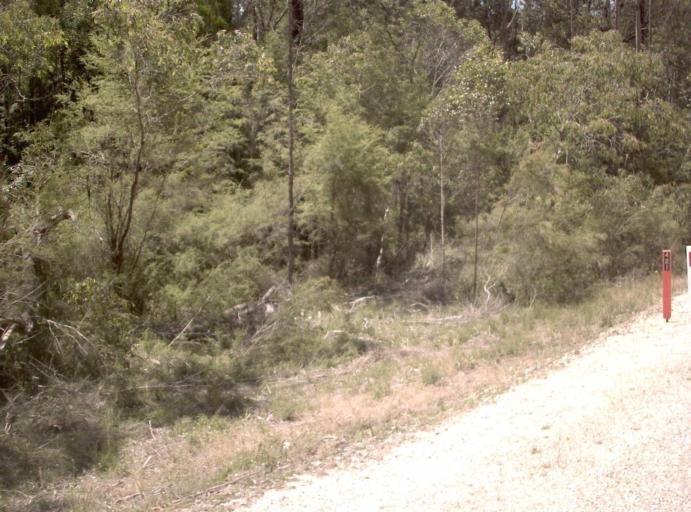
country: AU
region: New South Wales
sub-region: Bombala
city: Bombala
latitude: -37.6297
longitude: 148.8834
